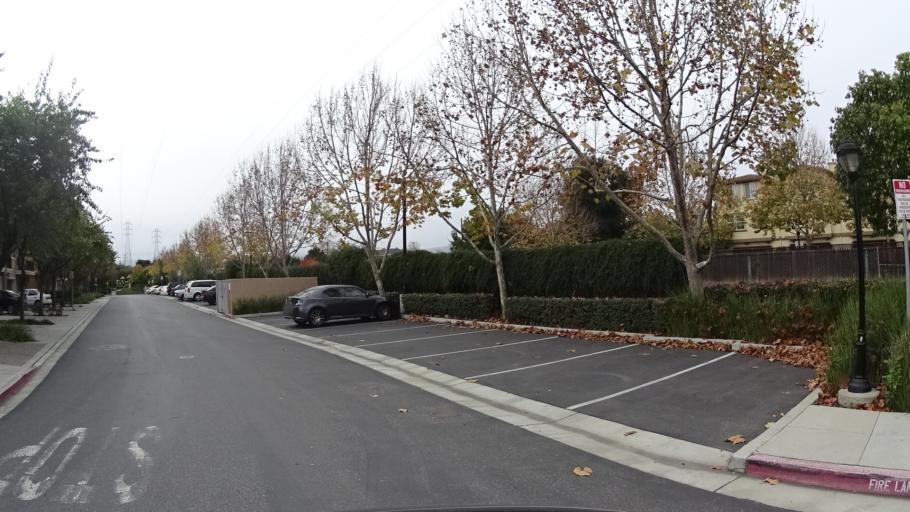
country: US
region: California
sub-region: Santa Clara County
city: Sunnyvale
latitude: 37.3723
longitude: -122.0177
